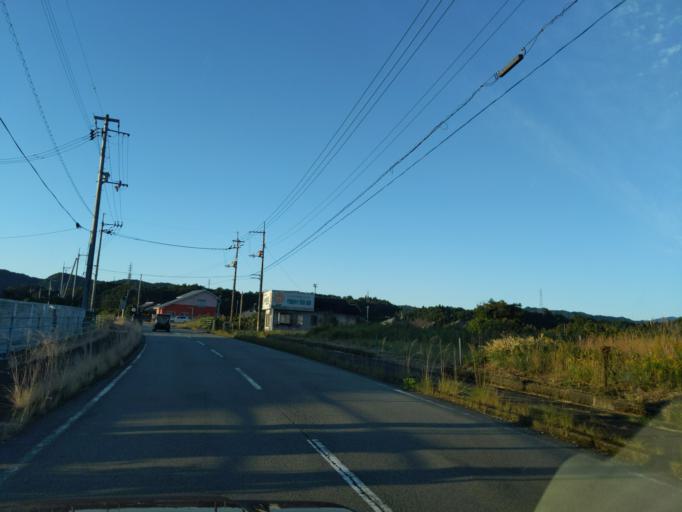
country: JP
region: Kochi
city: Muroto-misakicho
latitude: 33.6107
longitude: 134.3522
